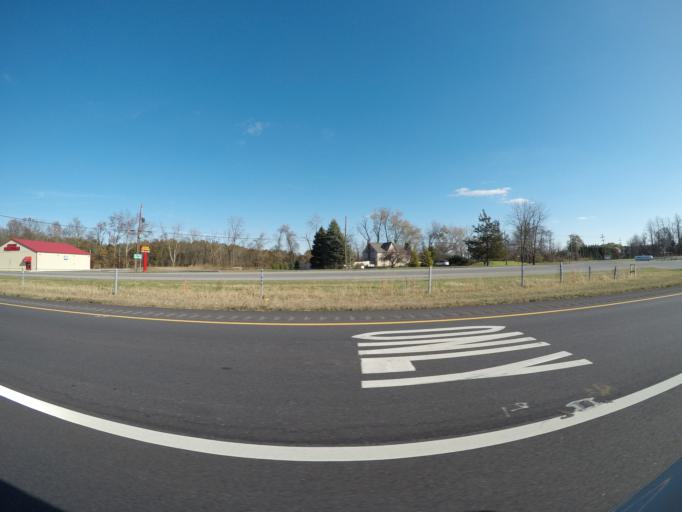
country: US
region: Maryland
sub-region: Cecil County
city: Rising Sun
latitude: 39.7248
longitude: -76.0287
